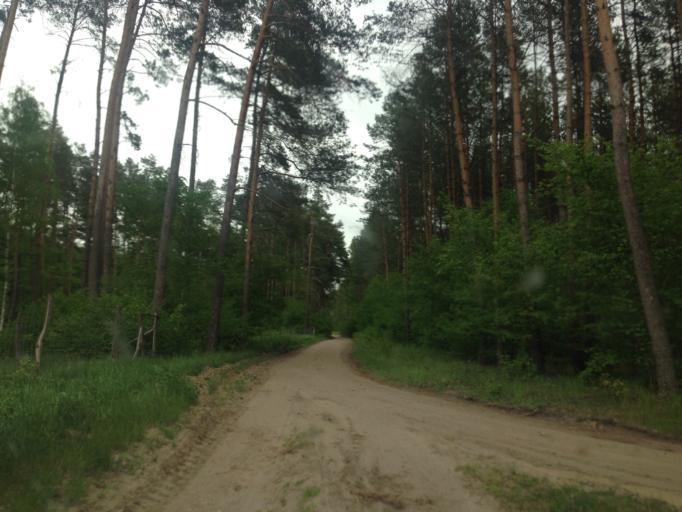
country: PL
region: Kujawsko-Pomorskie
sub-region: Powiat brodnicki
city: Bartniczka
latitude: 53.2674
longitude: 19.5596
